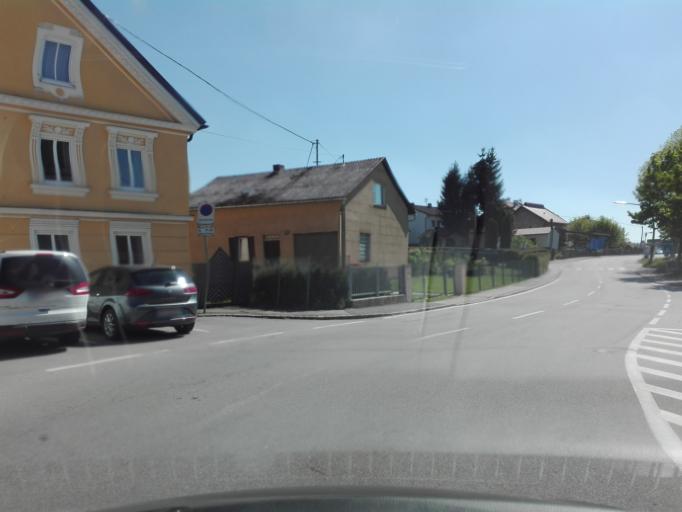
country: AT
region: Upper Austria
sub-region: Politischer Bezirk Grieskirchen
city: Grieskirchen
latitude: 48.3283
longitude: 13.8560
